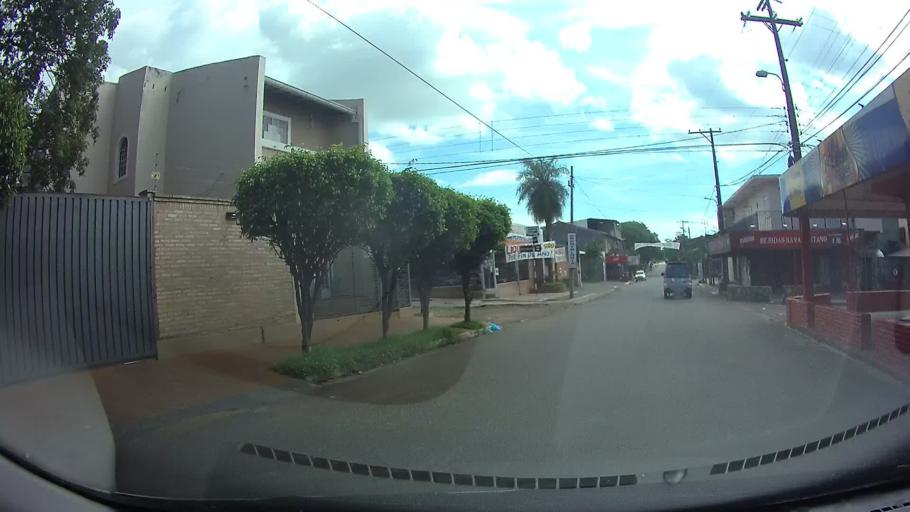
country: PY
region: Central
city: Villa Elisa
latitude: -25.3403
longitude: -57.5731
